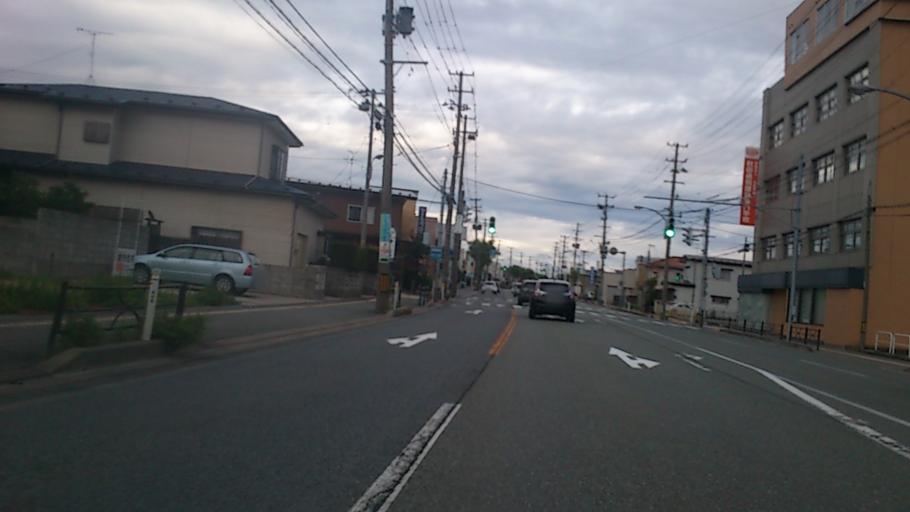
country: JP
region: Akita
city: Akita Shi
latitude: 39.7488
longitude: 140.0734
